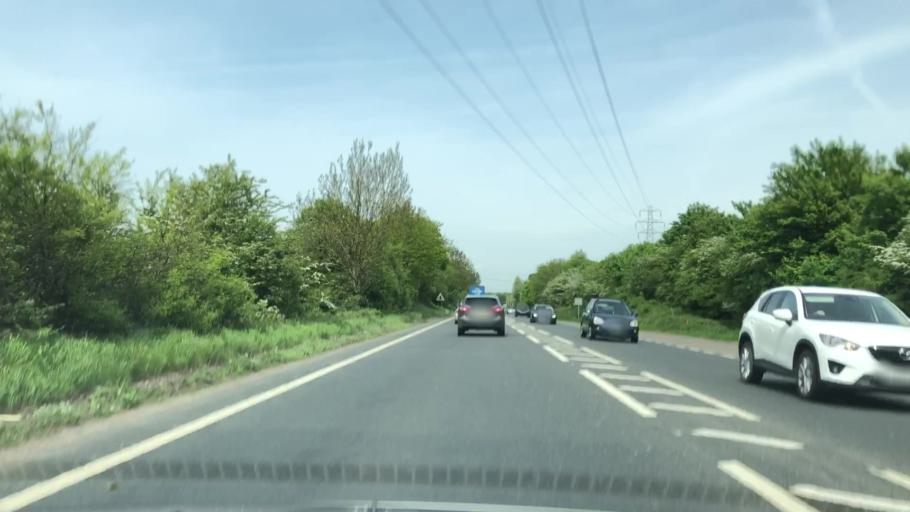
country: GB
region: England
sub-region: Shropshire
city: Gobowen
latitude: 52.9085
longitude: -3.0425
